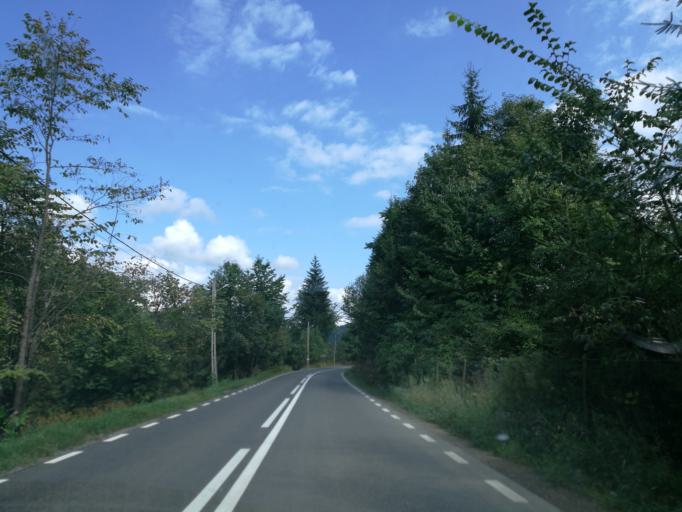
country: RO
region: Suceava
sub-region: Comuna Sucevita
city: Sucevita
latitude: 47.7608
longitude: 25.6827
